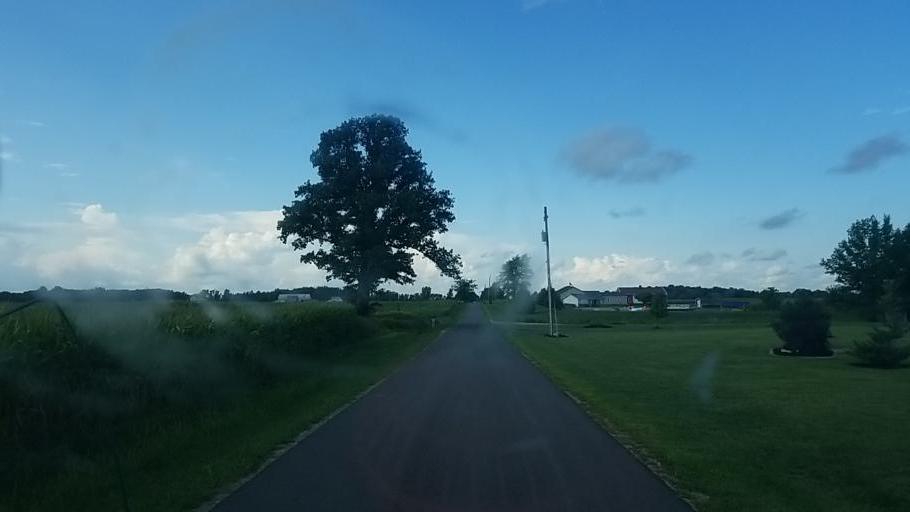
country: US
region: Ohio
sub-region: Hardin County
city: Forest
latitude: 40.7827
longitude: -83.4485
